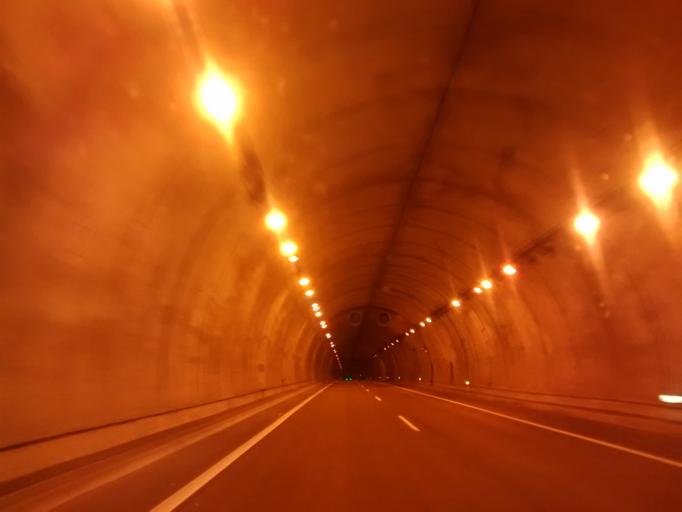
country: ES
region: Cantabria
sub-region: Provincia de Cantabria
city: Arenas de Iguna
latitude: 43.2040
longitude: -4.0732
